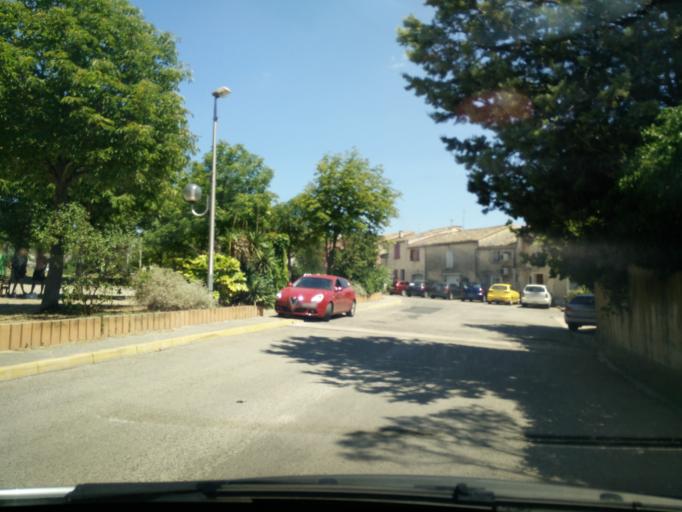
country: FR
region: Languedoc-Roussillon
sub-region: Departement de l'Herault
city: Villetelle
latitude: 43.7226
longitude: 4.1126
